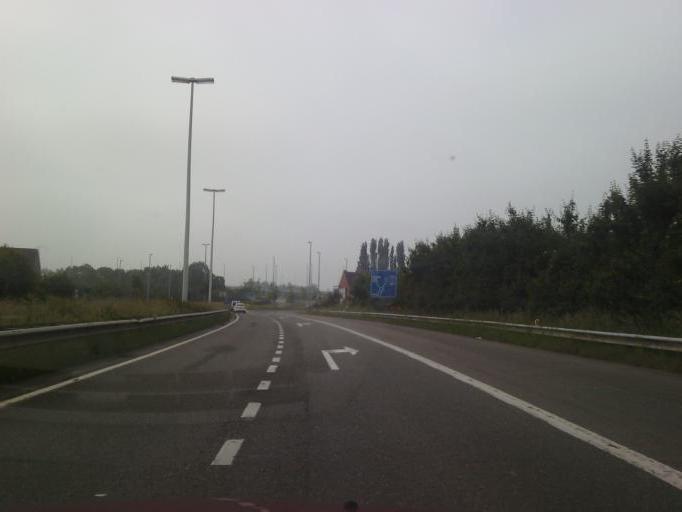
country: BE
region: Flanders
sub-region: Provincie Oost-Vlaanderen
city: Aalst
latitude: 50.9516
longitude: 4.0292
